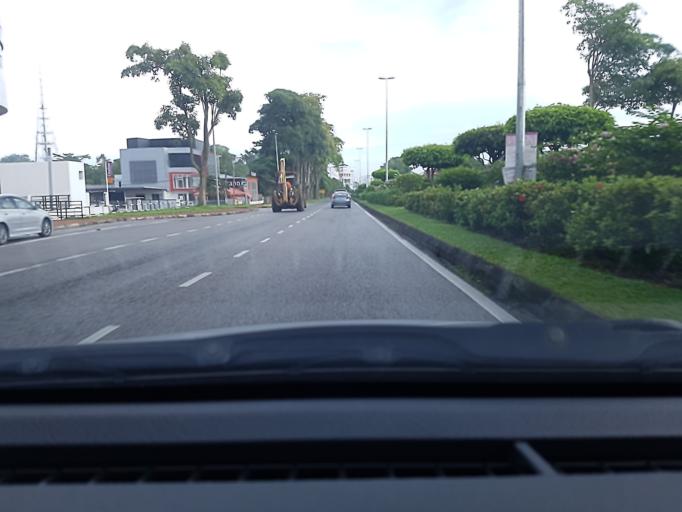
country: MY
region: Sarawak
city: Kuching
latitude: 1.5360
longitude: 110.3565
